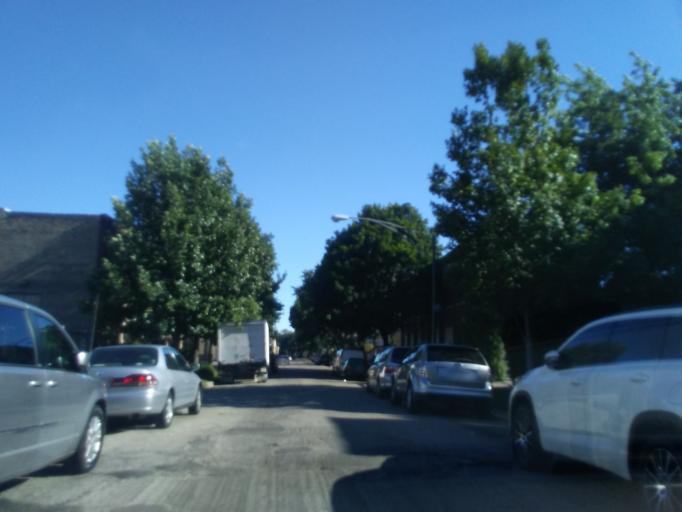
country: US
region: Illinois
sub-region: Cook County
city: Oak Park
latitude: 41.9231
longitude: -87.7426
